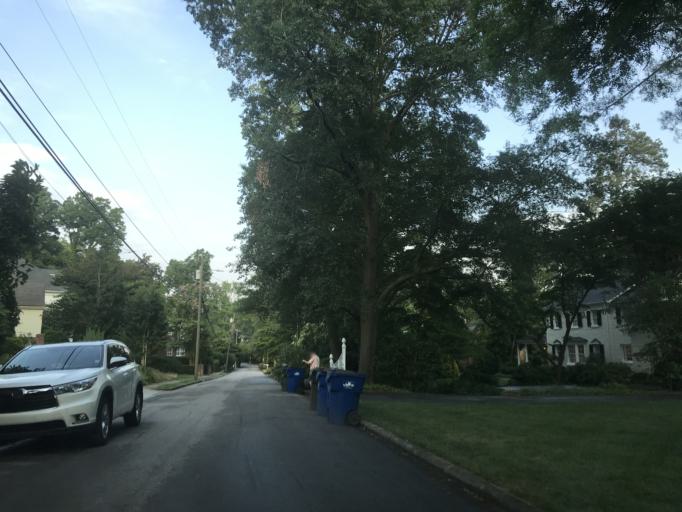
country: US
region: North Carolina
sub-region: Wake County
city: West Raleigh
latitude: 35.7993
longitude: -78.6559
